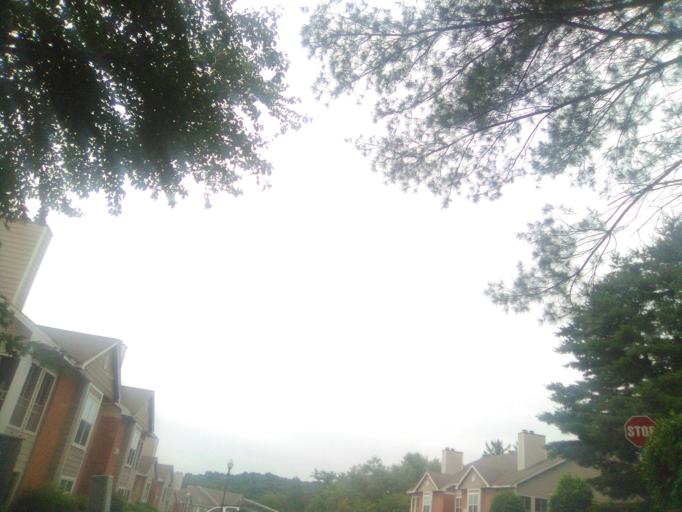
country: US
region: Tennessee
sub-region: Davidson County
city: Belle Meade
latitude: 36.0846
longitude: -86.8994
